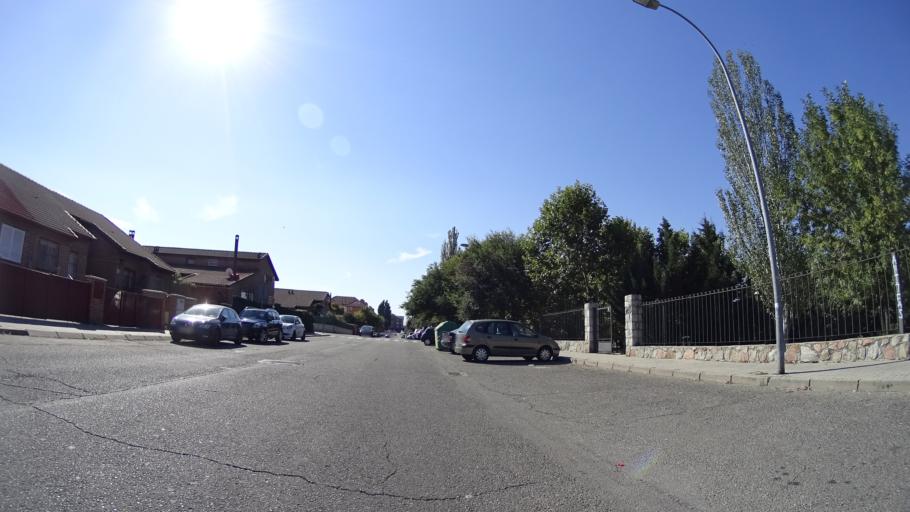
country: ES
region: Madrid
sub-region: Provincia de Madrid
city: Collado-Villalba
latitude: 40.6214
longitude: -4.0160
